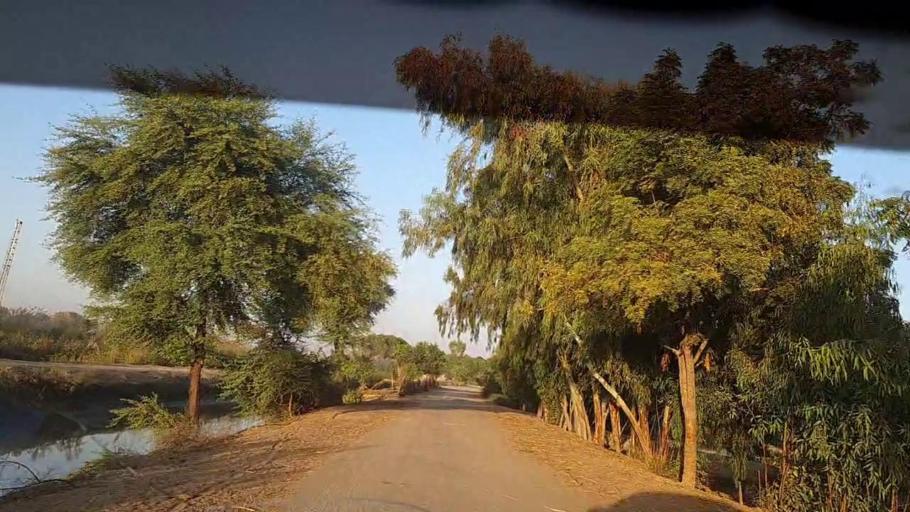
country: PK
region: Sindh
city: Ratodero
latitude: 27.9032
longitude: 68.2372
